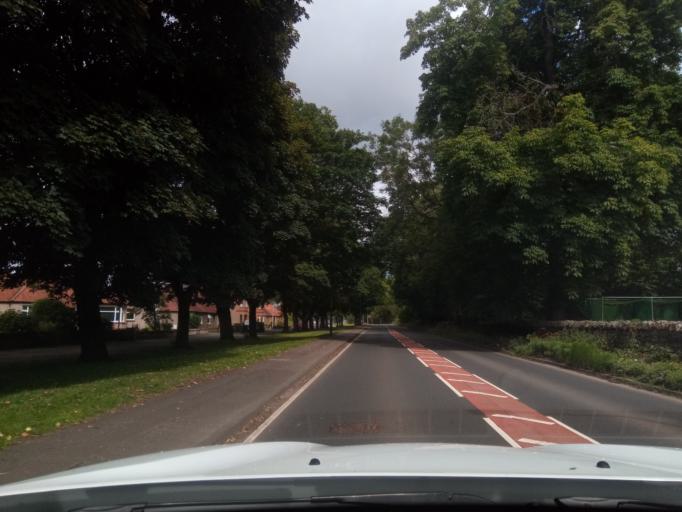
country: GB
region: Scotland
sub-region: Fife
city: Kincardine
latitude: 56.0773
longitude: -3.7206
